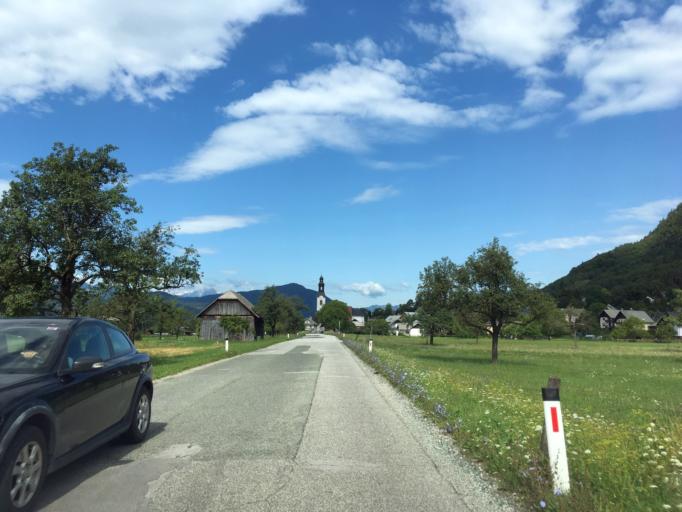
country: SI
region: Zirovnica
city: Zirovnica
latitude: 46.3938
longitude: 14.1590
